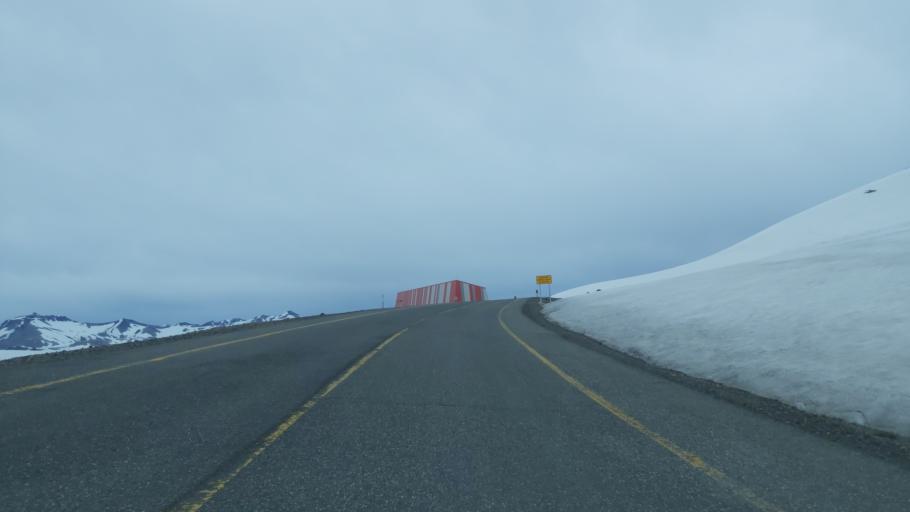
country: CL
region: Maule
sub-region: Provincia de Linares
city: Colbun
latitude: -36.0078
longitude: -70.4804
